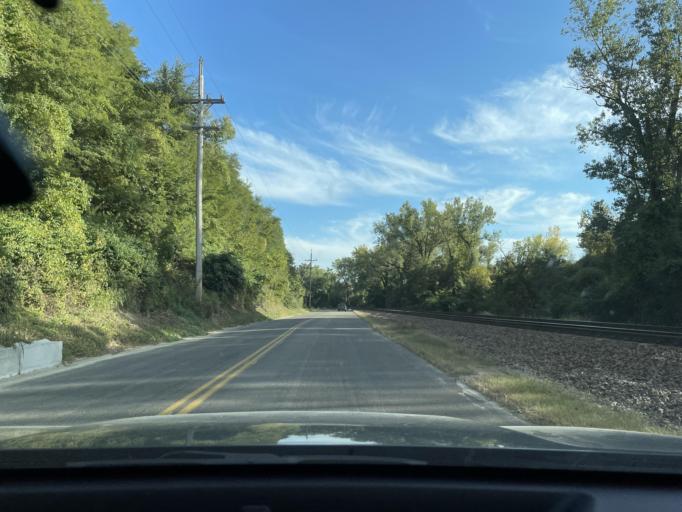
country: US
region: Missouri
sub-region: Buchanan County
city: Saint Joseph
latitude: 39.7722
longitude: -94.8644
